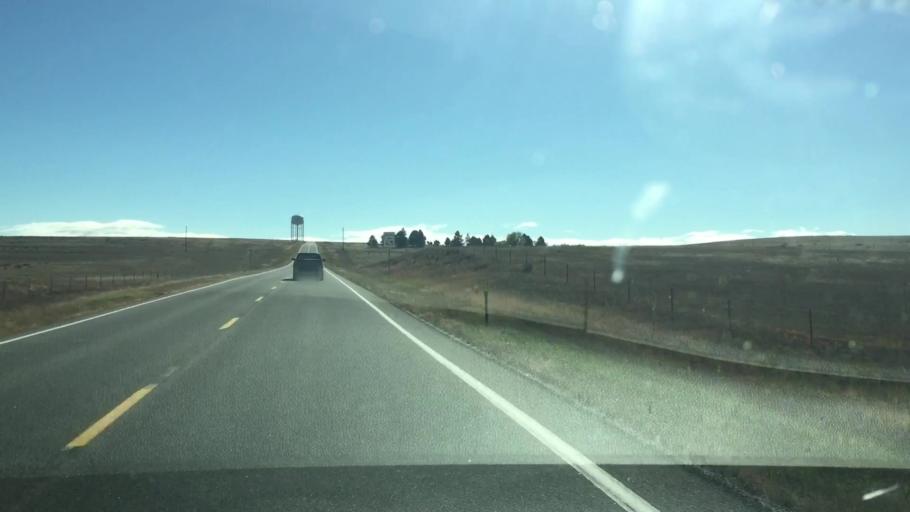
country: US
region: Colorado
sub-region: Elbert County
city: Kiowa
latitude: 39.3438
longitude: -104.4500
